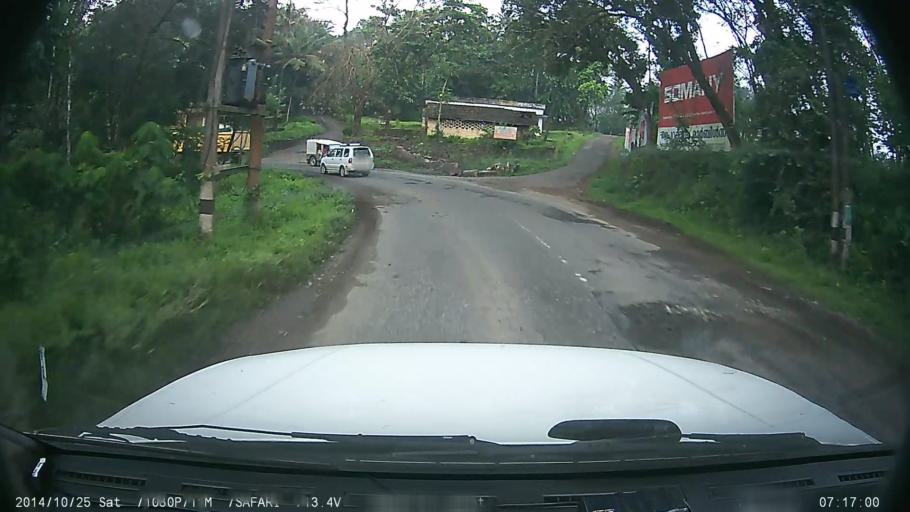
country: IN
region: Kerala
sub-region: Kottayam
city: Palackattumala
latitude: 9.8165
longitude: 76.5857
